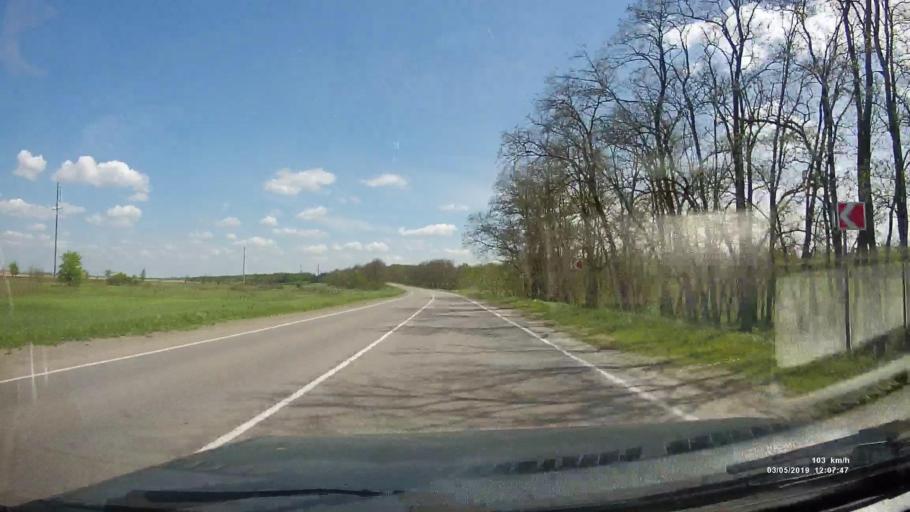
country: RU
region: Rostov
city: Bagayevskaya
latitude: 47.2843
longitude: 40.4830
